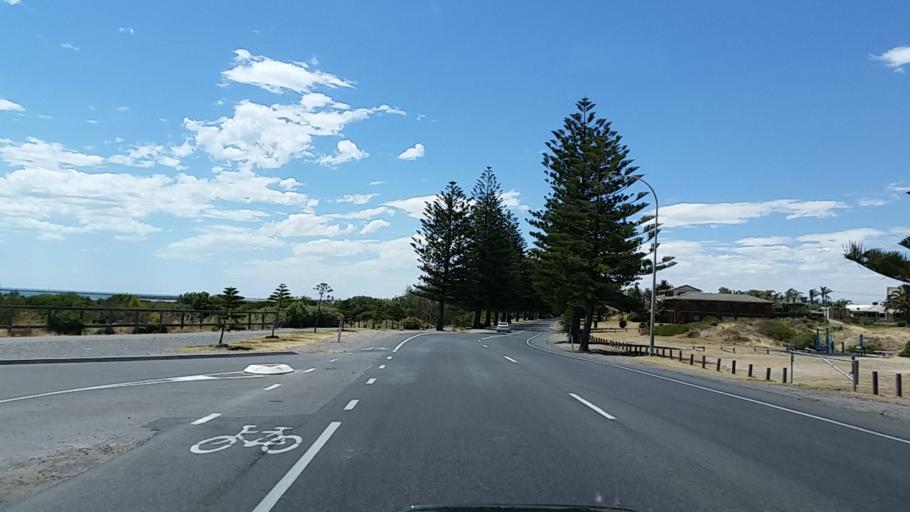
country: AU
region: South Australia
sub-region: Port Adelaide Enfield
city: Birkenhead
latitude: -34.8091
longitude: 138.4913
